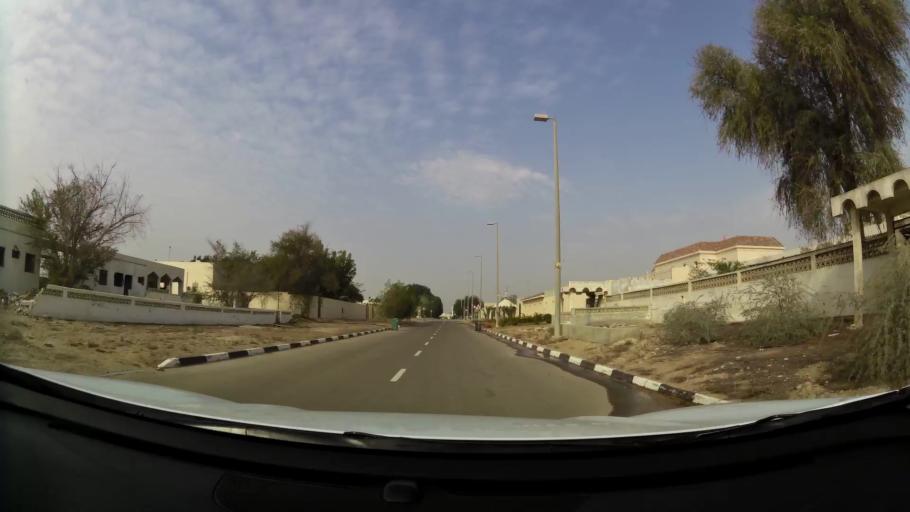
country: AE
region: Abu Dhabi
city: Abu Dhabi
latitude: 24.6793
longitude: 54.7766
